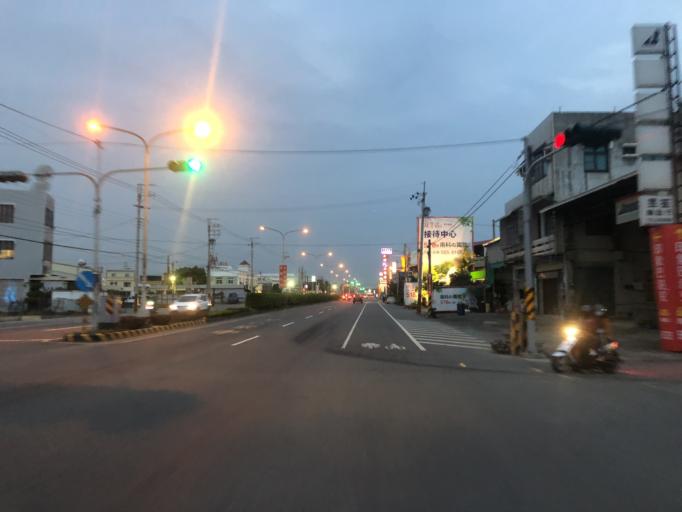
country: TW
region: Taiwan
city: Yujing
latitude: 23.1352
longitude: 120.3220
